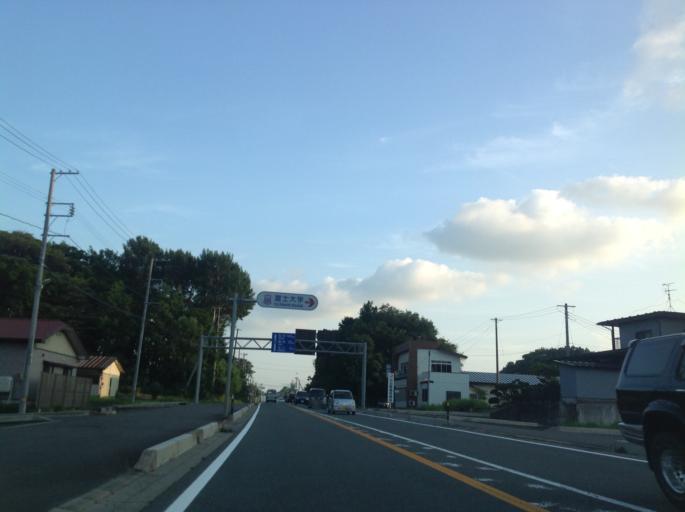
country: JP
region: Iwate
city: Hanamaki
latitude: 39.3616
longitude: 141.1137
